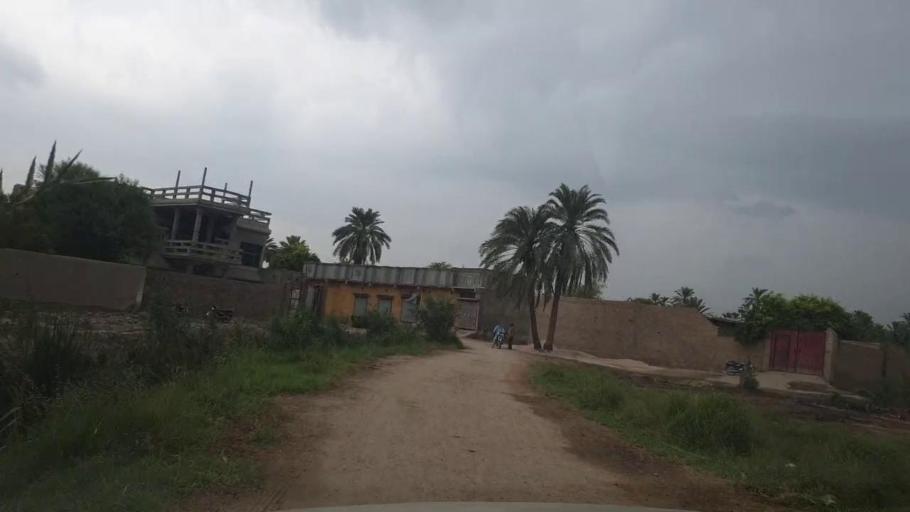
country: PK
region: Sindh
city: Khairpur
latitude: 27.5380
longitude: 68.7364
